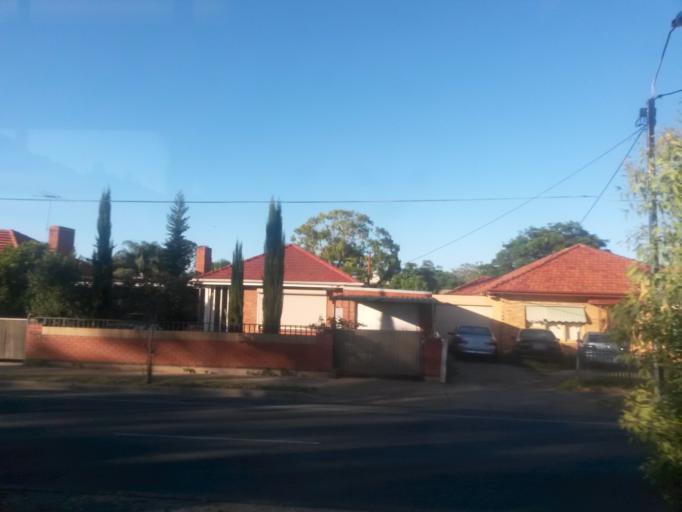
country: AU
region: South Australia
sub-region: Charles Sturt
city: Woodville North
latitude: -34.8711
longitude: 138.5416
